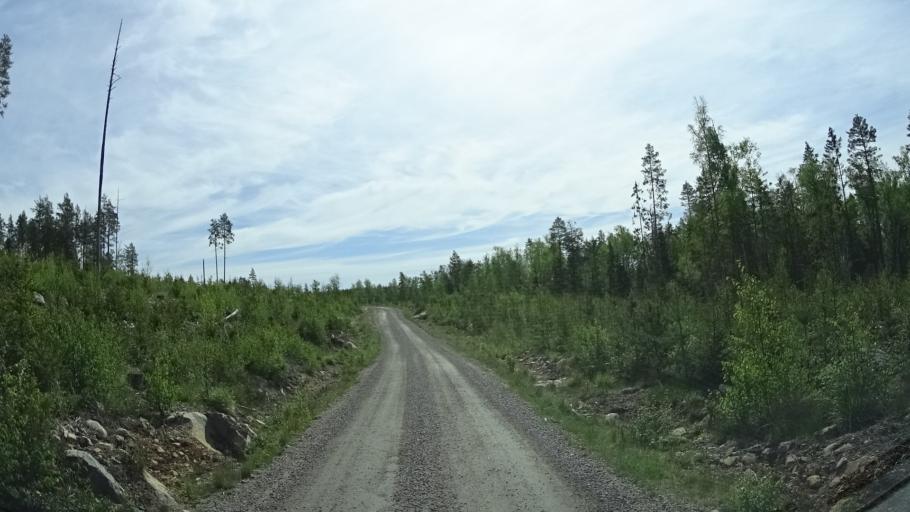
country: SE
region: OEstergoetland
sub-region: Finspangs Kommun
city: Finspang
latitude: 58.7799
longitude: 15.8577
